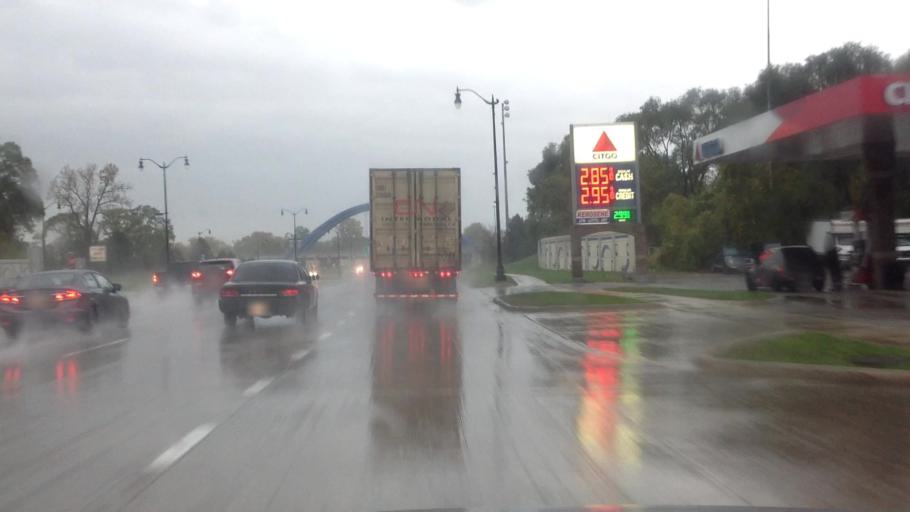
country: US
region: Michigan
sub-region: Wayne County
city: Taylor
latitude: 42.2602
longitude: -83.2702
